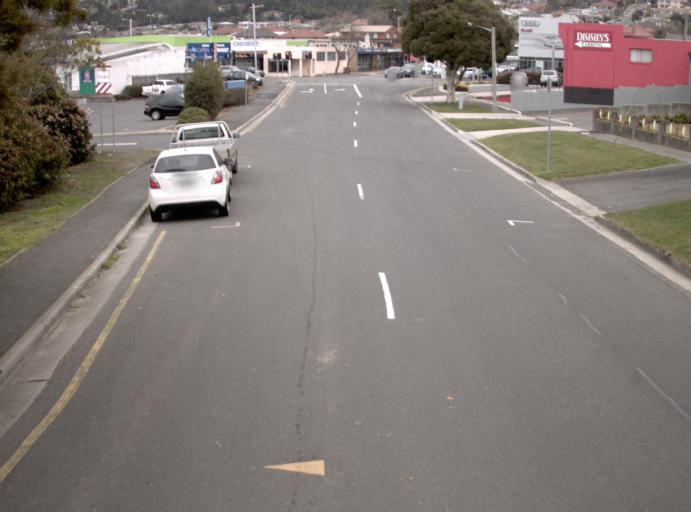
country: AU
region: Tasmania
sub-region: Launceston
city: East Launceston
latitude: -41.4639
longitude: 147.1597
